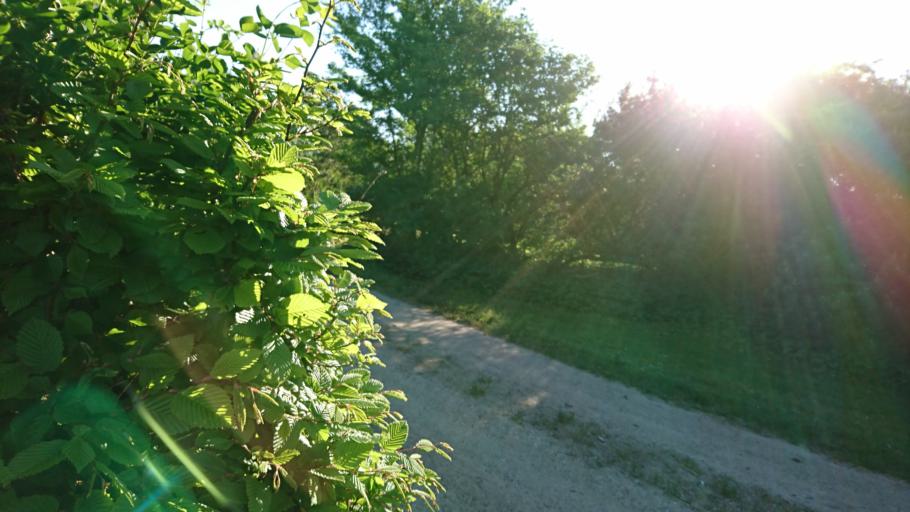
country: DK
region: Capital Region
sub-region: Ballerup Kommune
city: Ballerup
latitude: 55.7097
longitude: 12.3751
